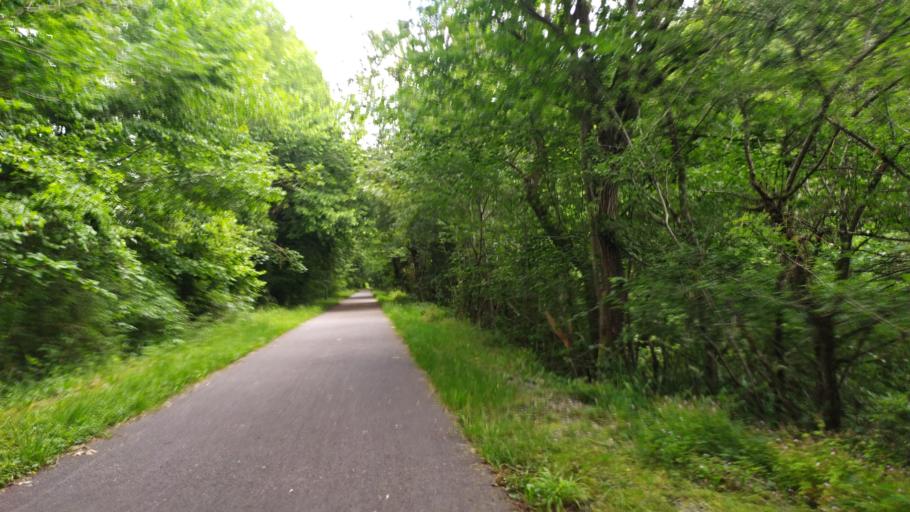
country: BE
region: Wallonia
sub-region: Province de Namur
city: Rochefort
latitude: 50.1566
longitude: 5.2327
